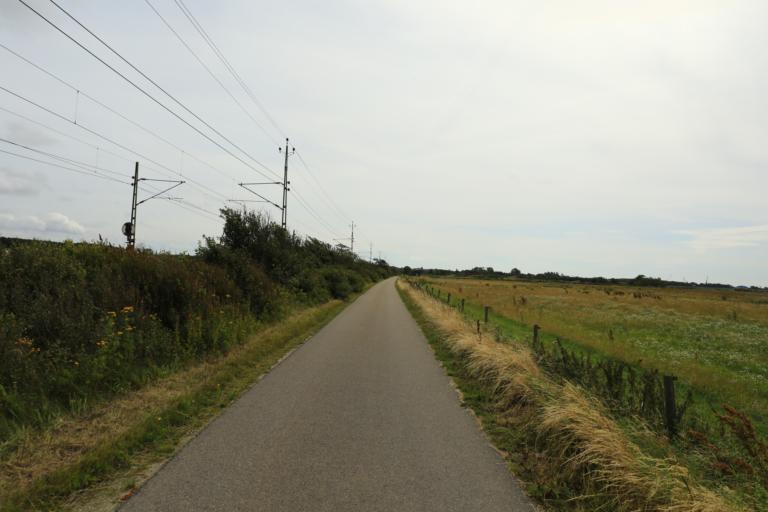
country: SE
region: Halland
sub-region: Varbergs Kommun
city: Varberg
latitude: 57.1384
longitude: 12.2588
